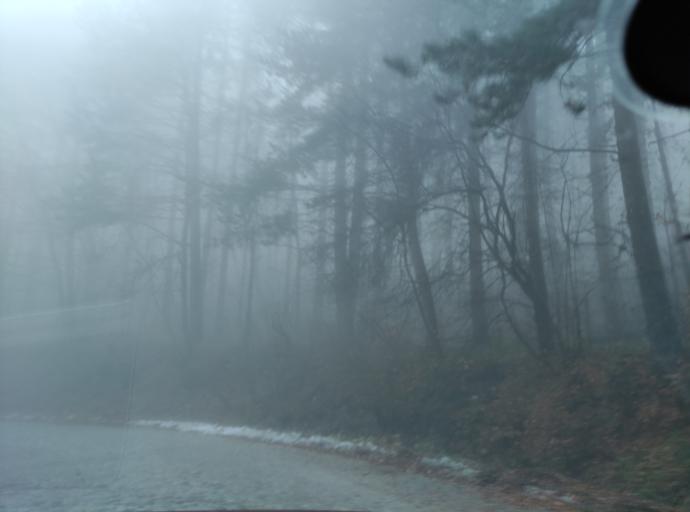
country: BG
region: Sofia-Capital
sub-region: Stolichna Obshtina
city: Sofia
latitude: 42.6187
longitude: 23.2945
